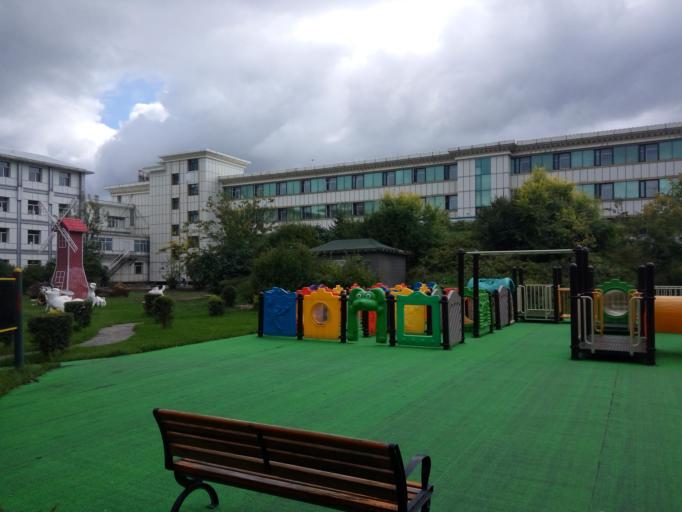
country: CN
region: Heilongjiang Sheng
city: Erjing
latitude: 48.6503
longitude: 126.1413
